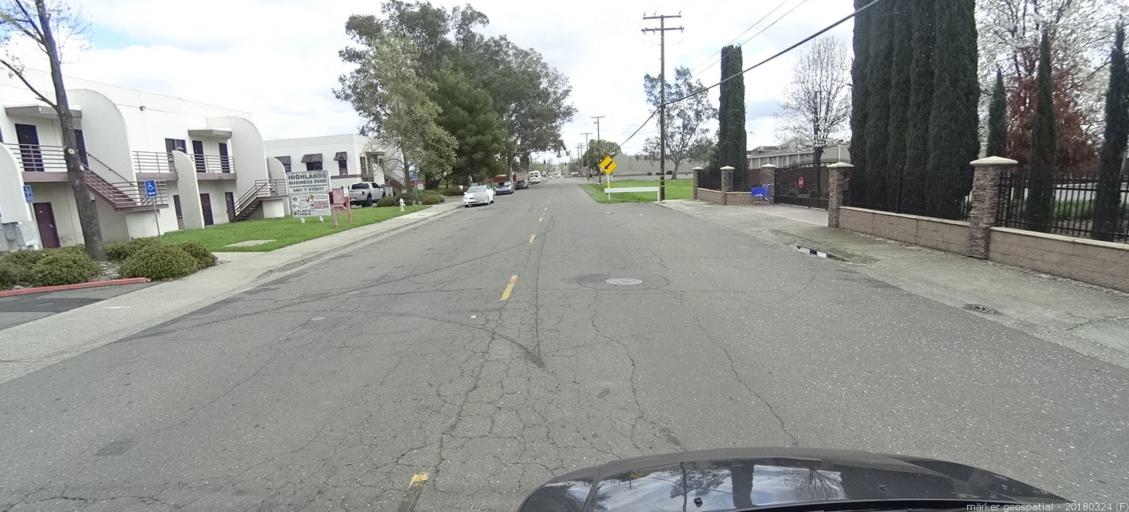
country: US
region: California
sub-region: Sacramento County
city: North Highlands
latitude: 38.6831
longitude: -121.3857
